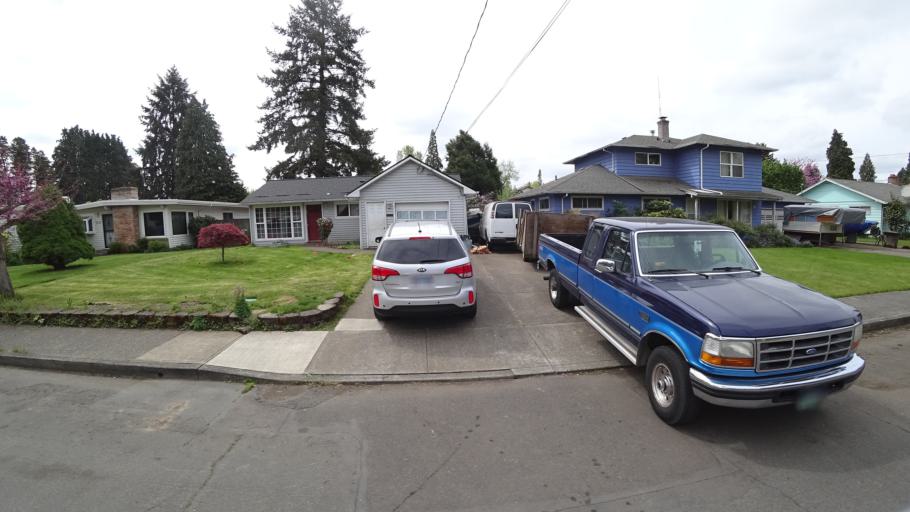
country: US
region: Oregon
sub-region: Washington County
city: Hillsboro
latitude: 45.5285
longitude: -122.9921
